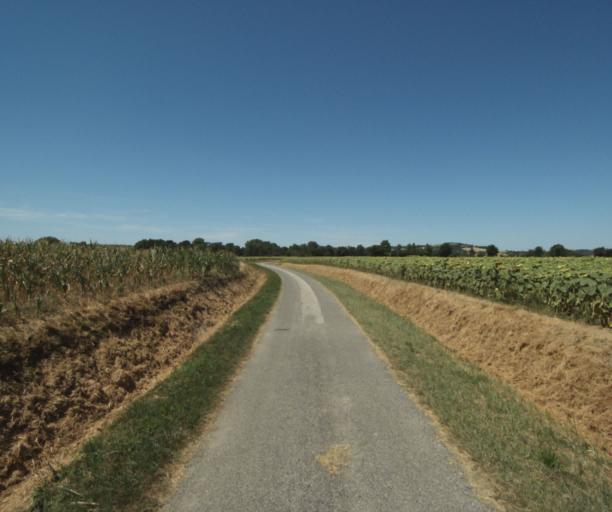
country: FR
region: Midi-Pyrenees
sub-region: Departement de la Haute-Garonne
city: Revel
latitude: 43.4763
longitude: 1.9485
